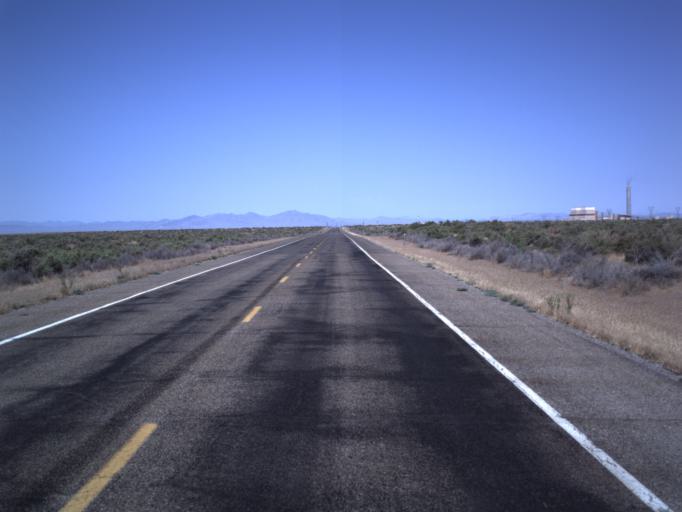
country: US
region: Utah
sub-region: Millard County
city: Delta
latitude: 39.4839
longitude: -112.5259
